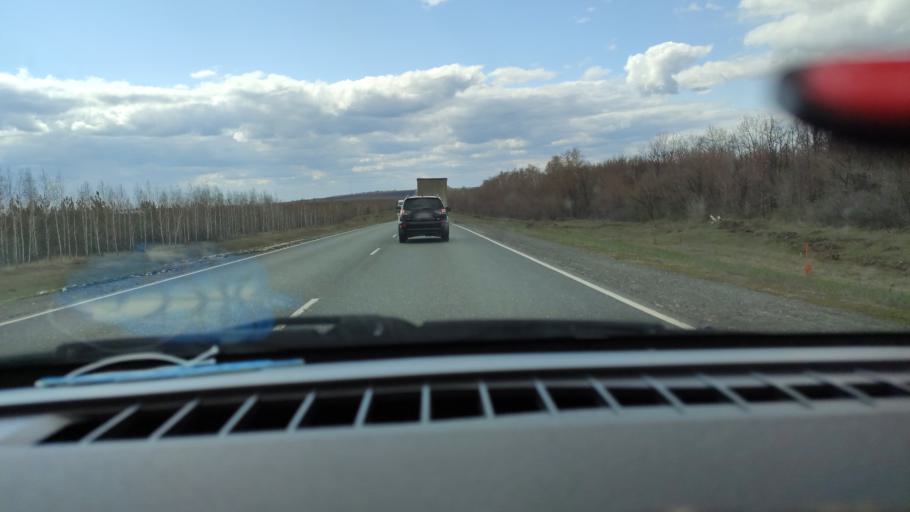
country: RU
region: Saratov
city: Balakovo
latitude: 52.1478
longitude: 47.8082
